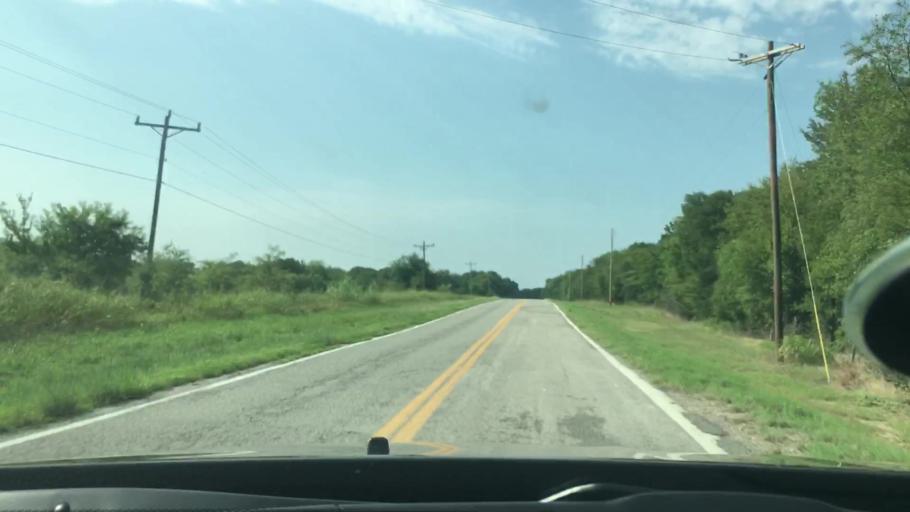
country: US
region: Oklahoma
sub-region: Johnston County
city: Tishomingo
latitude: 34.1766
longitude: -96.5838
